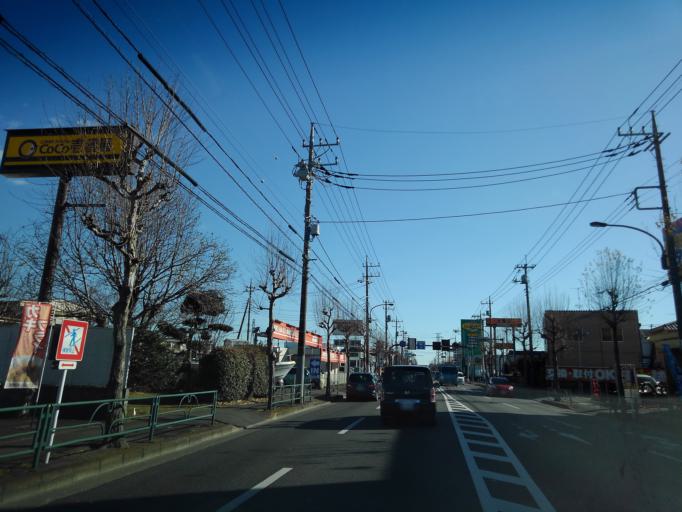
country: JP
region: Tokyo
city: Fussa
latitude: 35.7616
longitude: 139.3611
